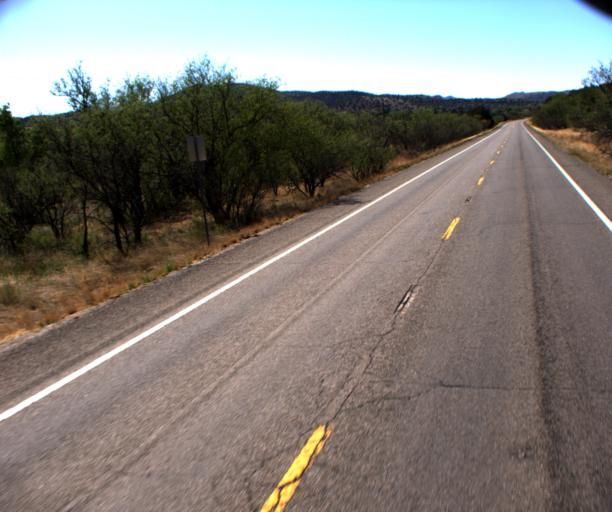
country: US
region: Arizona
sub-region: Santa Cruz County
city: Rio Rico
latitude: 31.6405
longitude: -110.7141
